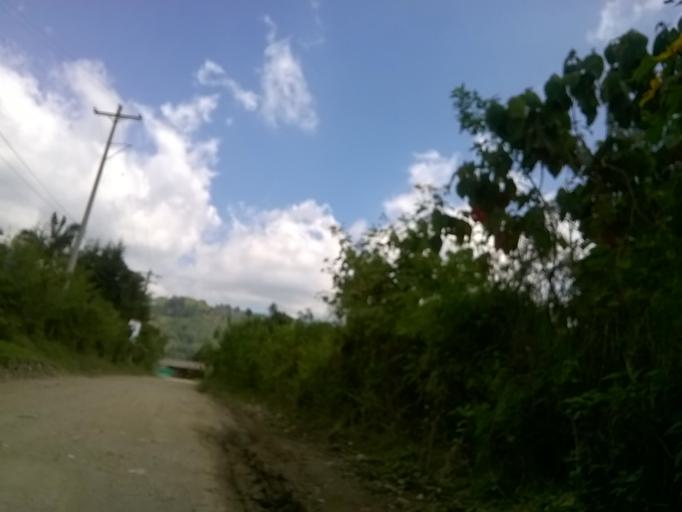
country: CO
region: Quindio
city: Circasia
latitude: 4.5907
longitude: -75.6317
